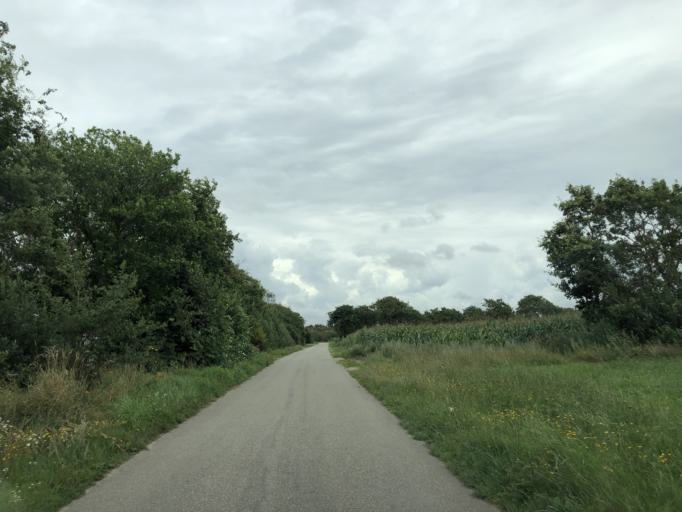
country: DK
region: Central Jutland
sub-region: Ringkobing-Skjern Kommune
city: Ringkobing
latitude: 56.1313
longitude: 8.2563
